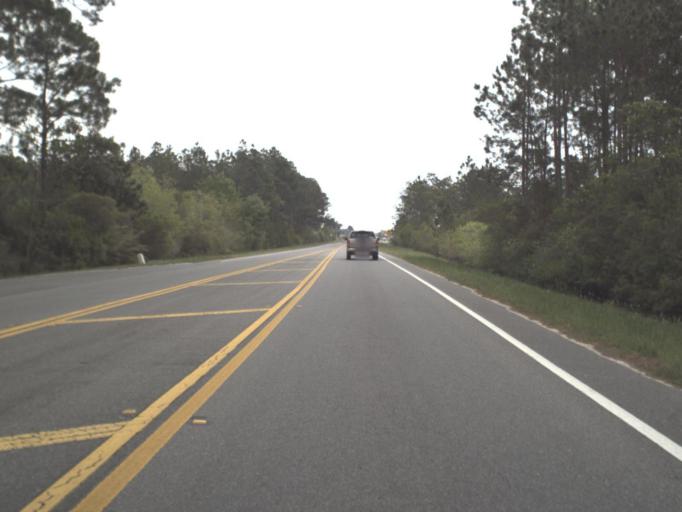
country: US
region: Florida
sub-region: Escambia County
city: Myrtle Grove
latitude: 30.4035
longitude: -87.3497
